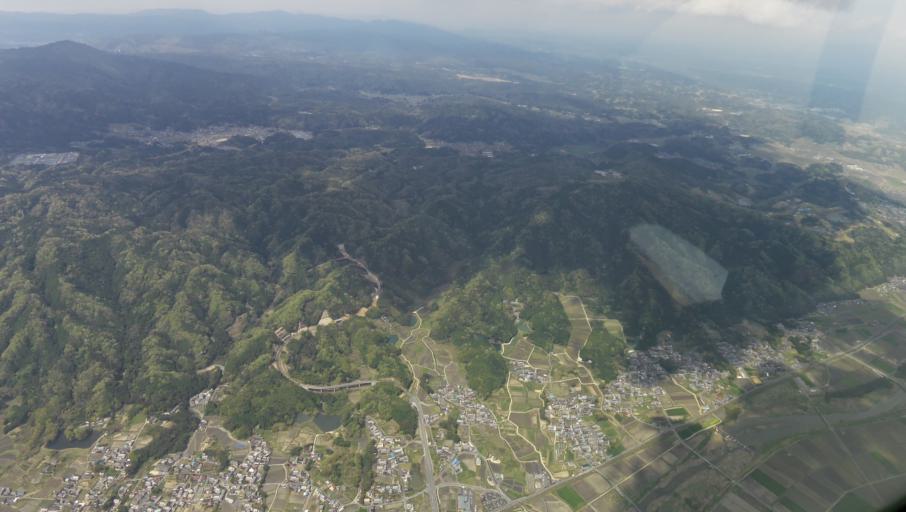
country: JP
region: Mie
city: Ueno-ebisumachi
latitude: 34.7851
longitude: 136.1361
